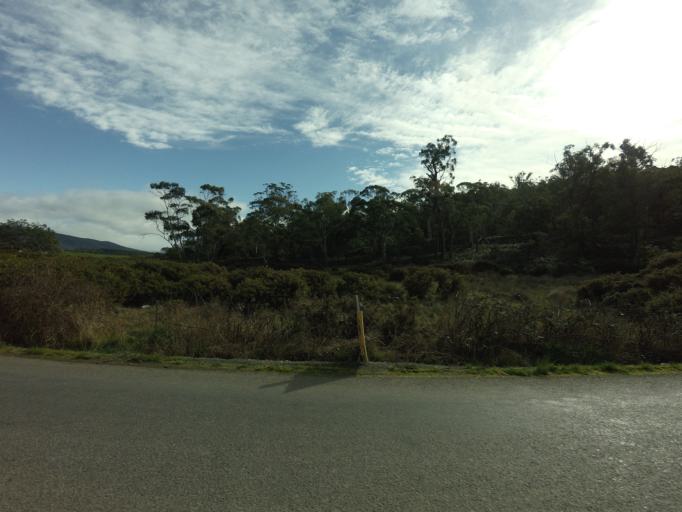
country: AU
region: Tasmania
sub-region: Derwent Valley
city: New Norfolk
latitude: -42.7815
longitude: 147.0032
